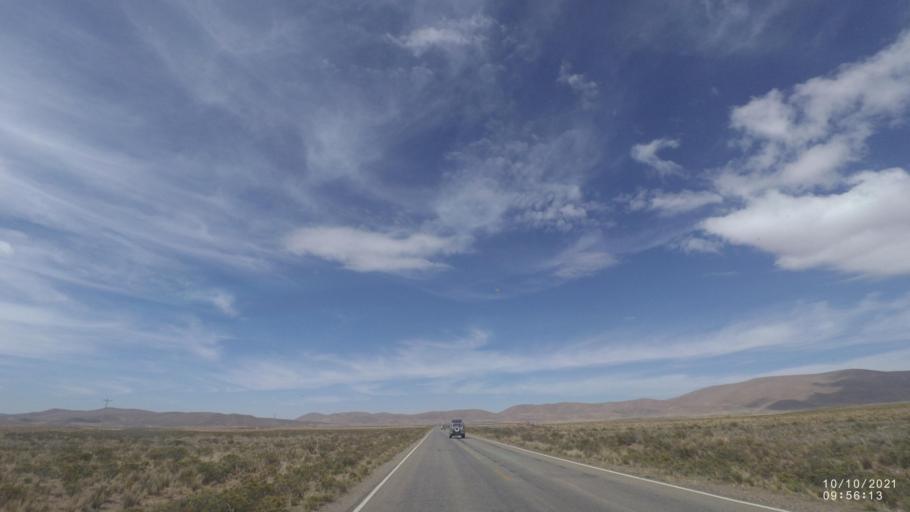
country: BO
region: La Paz
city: Colquiri
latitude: -17.3192
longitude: -67.3729
